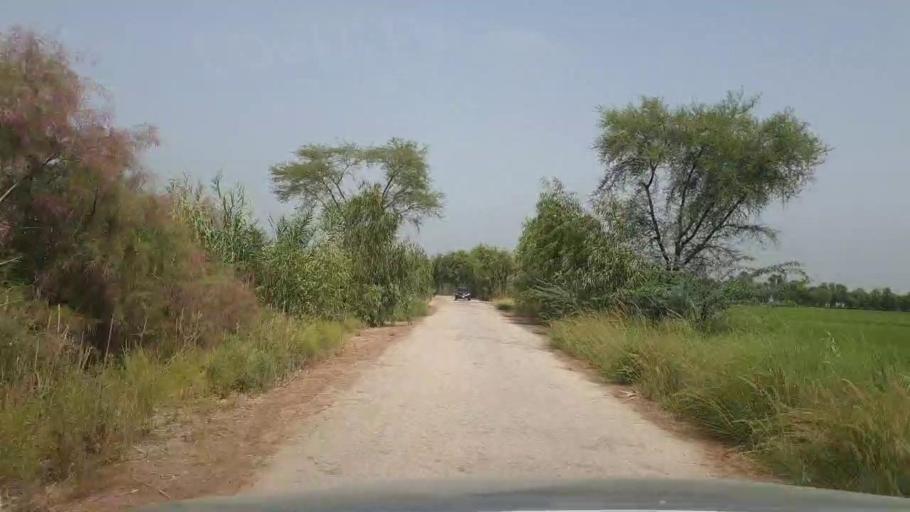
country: PK
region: Sindh
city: Garhi Yasin
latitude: 27.9459
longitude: 68.3724
